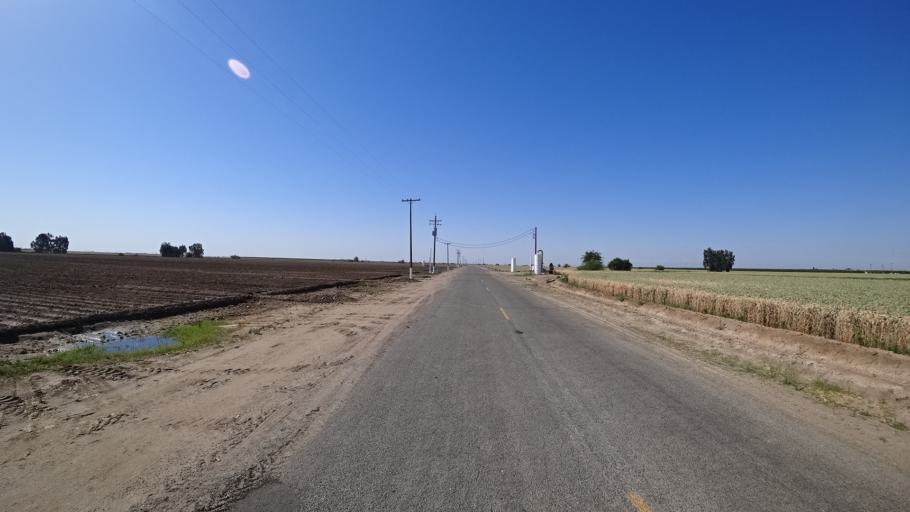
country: US
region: California
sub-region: Kings County
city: Home Garden
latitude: 36.2209
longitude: -119.5651
